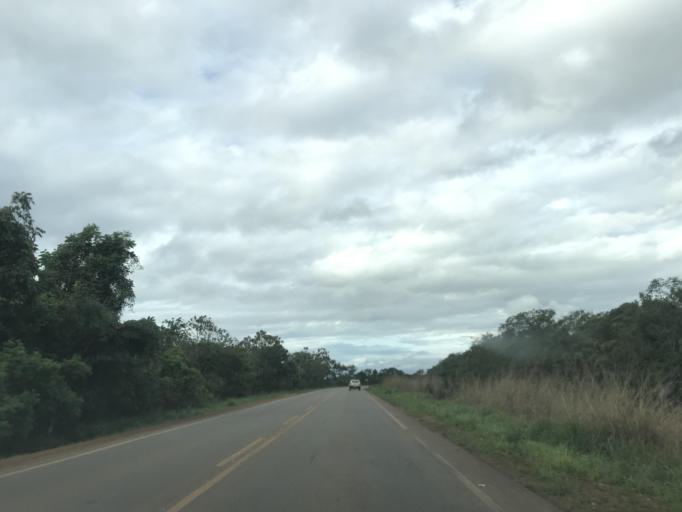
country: BR
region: Goias
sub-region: Vianopolis
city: Vianopolis
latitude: -16.7355
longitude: -48.4462
